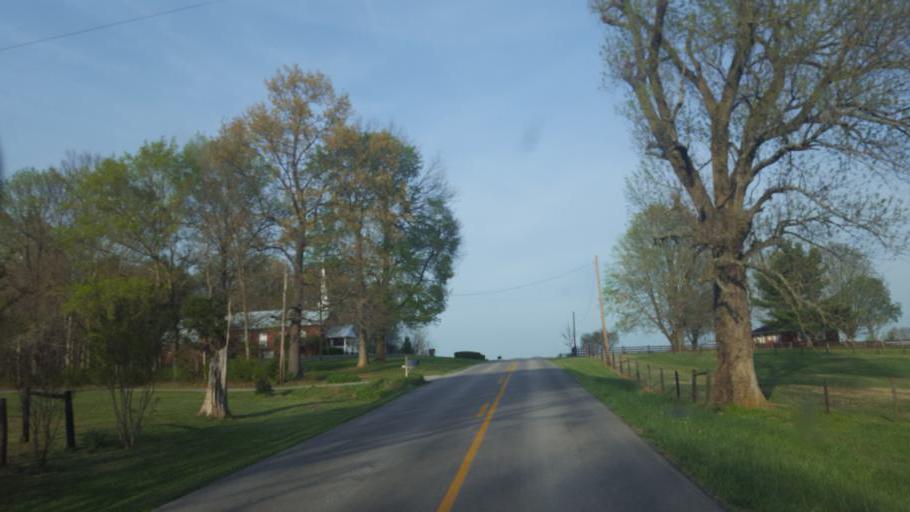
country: US
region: Kentucky
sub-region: Barren County
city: Glasgow
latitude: 36.9407
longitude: -86.0602
